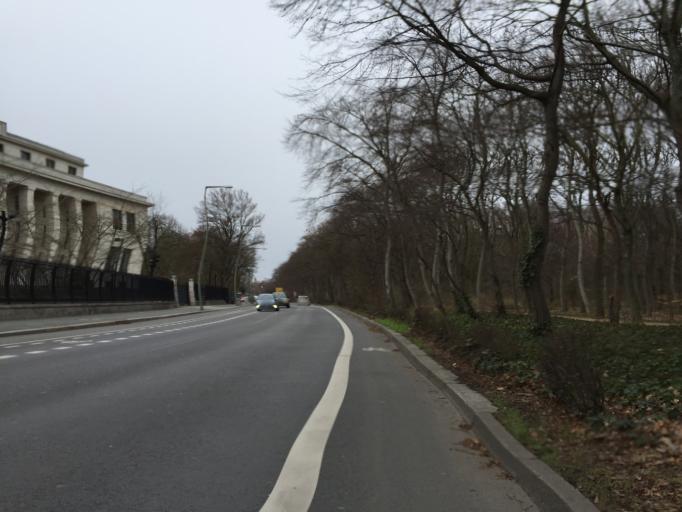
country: DE
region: Berlin
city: Tiergarten Bezirk
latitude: 52.5099
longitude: 13.3588
